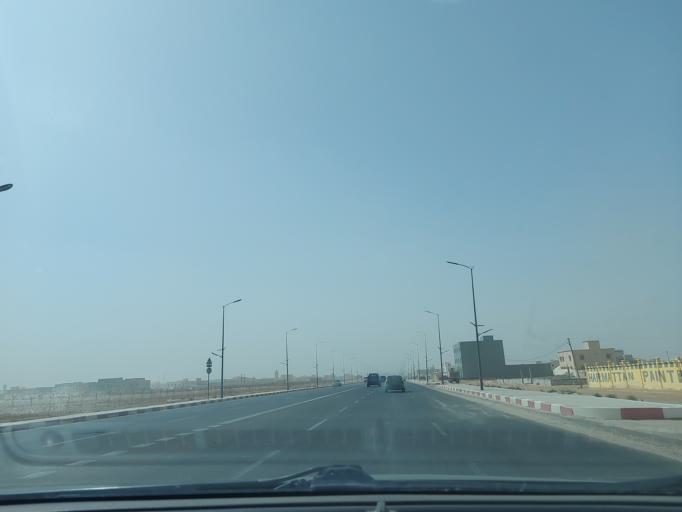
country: MR
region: Nouakchott
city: Nouakchott
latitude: 18.1361
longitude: -16.0050
